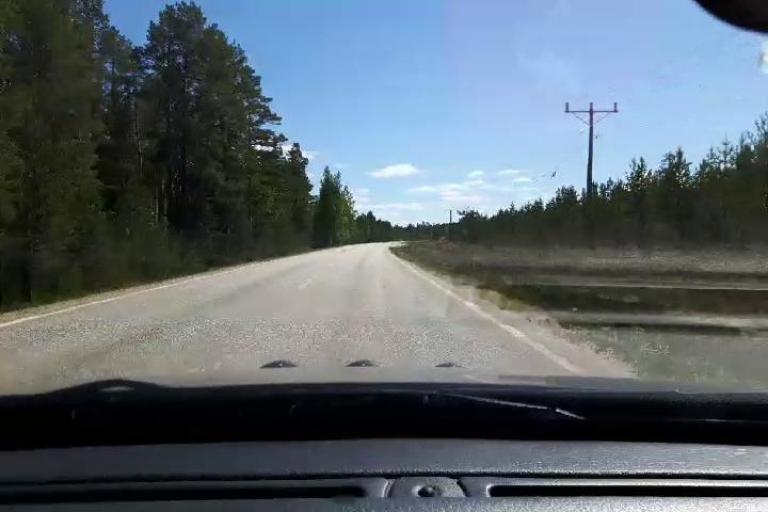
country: SE
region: Jaemtland
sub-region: Harjedalens Kommun
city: Sveg
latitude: 62.1097
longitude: 15.0611
